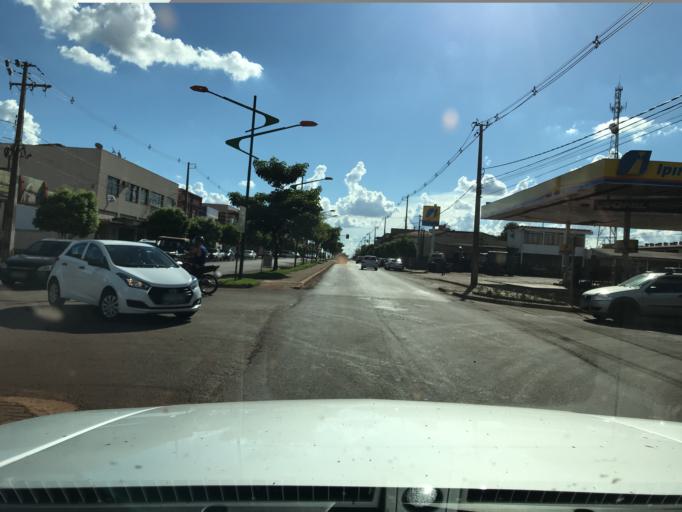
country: BR
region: Parana
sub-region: Palotina
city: Palotina
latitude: -24.2819
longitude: -53.8352
